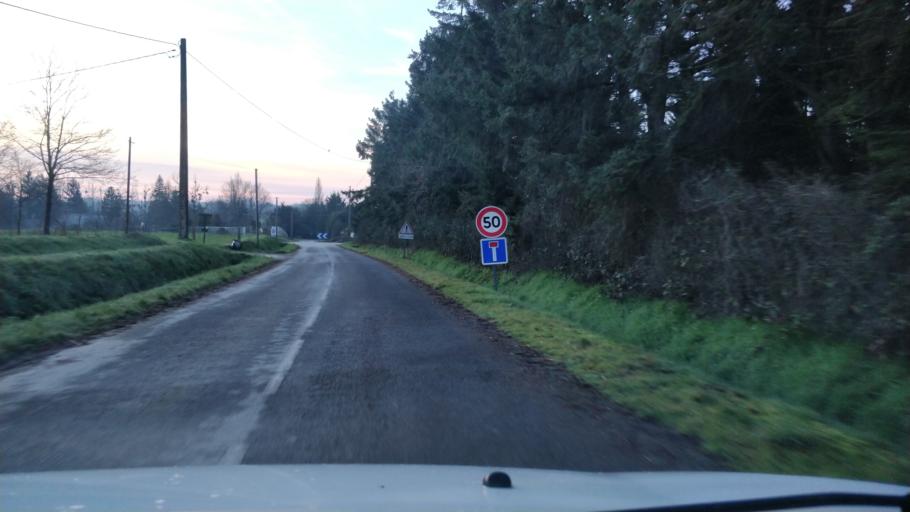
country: FR
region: Brittany
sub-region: Departement d'Ille-et-Vilaine
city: Louvigne-de-Bais
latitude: 48.0428
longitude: -1.3276
